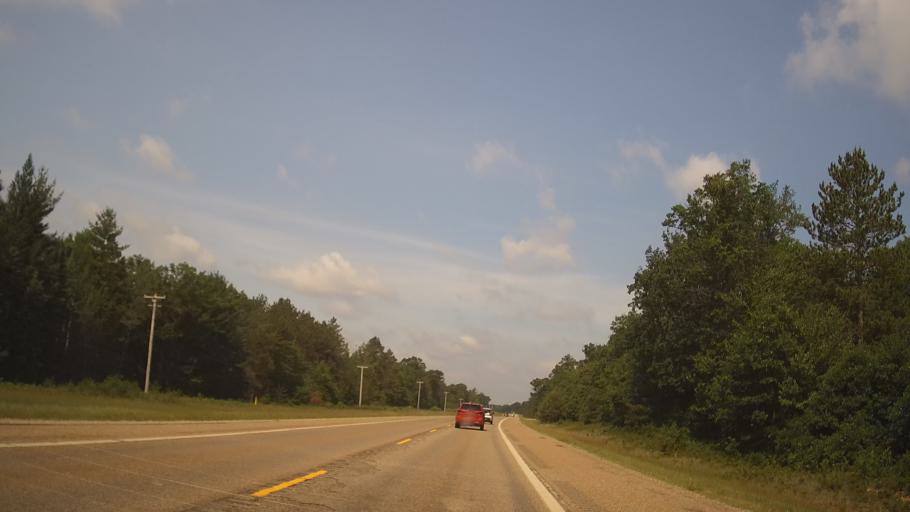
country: US
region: Michigan
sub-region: Roscommon County
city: Prudenville
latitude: 44.3043
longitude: -84.5768
